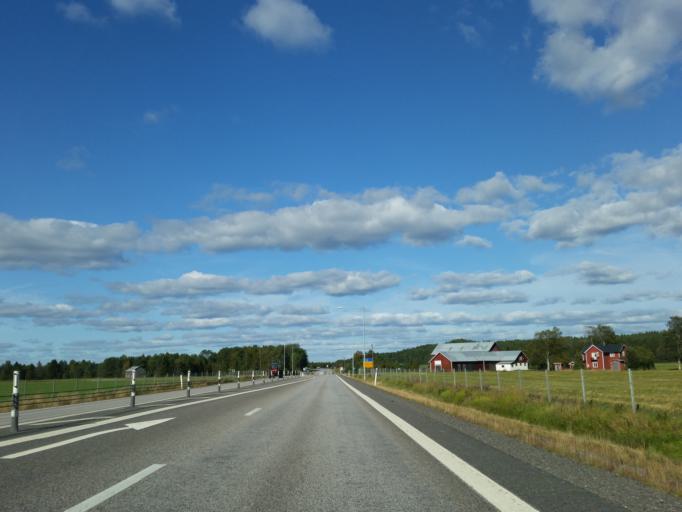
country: SE
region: Vaesterbotten
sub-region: Robertsfors Kommun
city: Robertsfors
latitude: 64.1265
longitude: 20.8863
